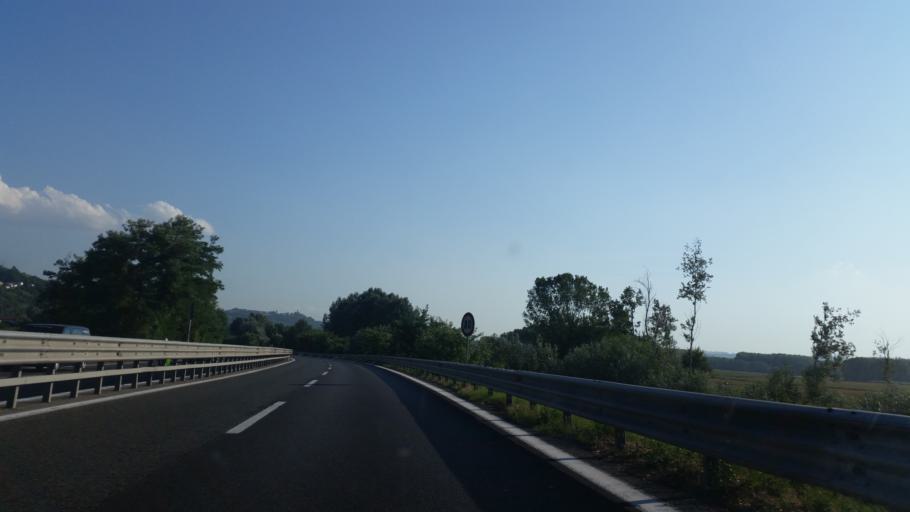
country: IT
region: Piedmont
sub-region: Provincia di Asti
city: Mongardino
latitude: 44.8708
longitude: 8.2074
